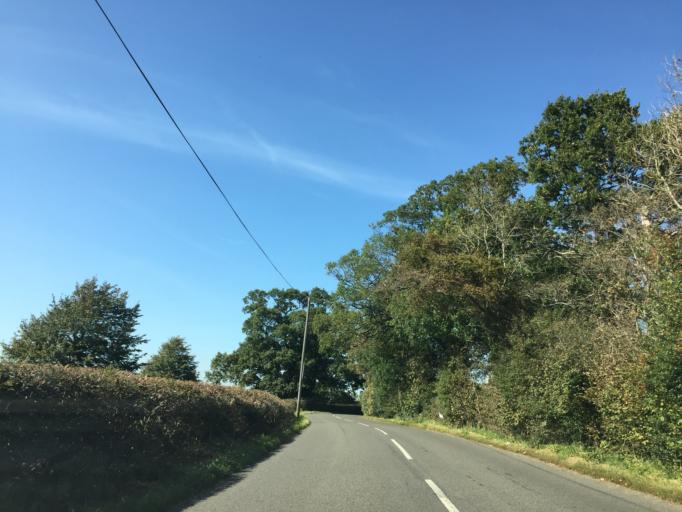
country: GB
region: England
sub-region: Leicestershire
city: Houghton on the Hill
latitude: 52.6749
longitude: -0.9375
